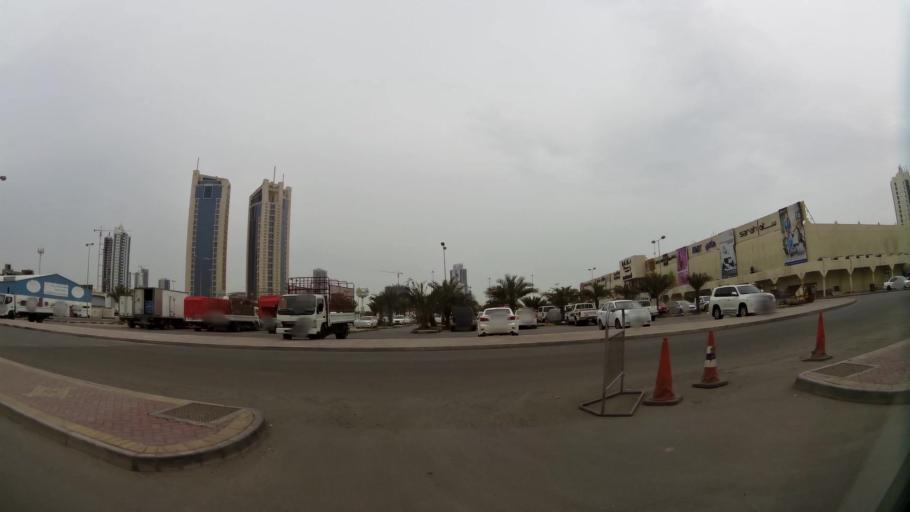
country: BH
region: Manama
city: Jidd Hafs
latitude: 26.2280
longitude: 50.5642
